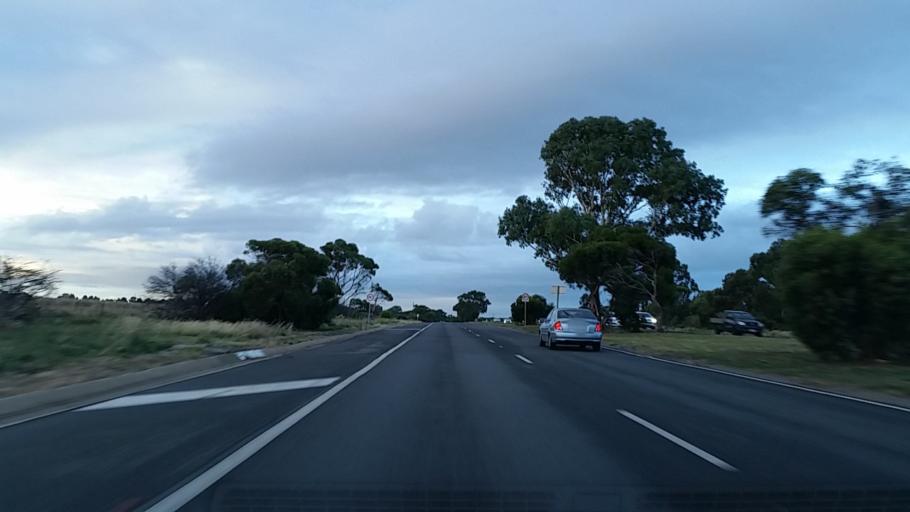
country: AU
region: South Australia
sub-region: Marion
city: Trott Park
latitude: -35.0683
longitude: 138.5293
